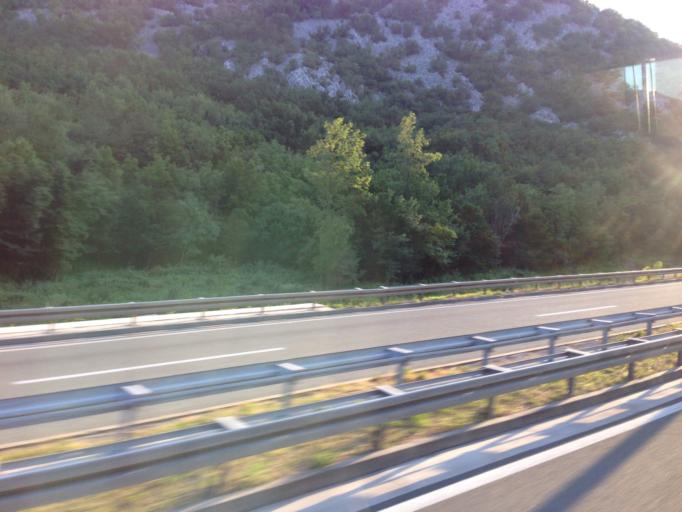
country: HR
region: Primorsko-Goranska
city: Skrljevo
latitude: 45.3185
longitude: 14.5016
